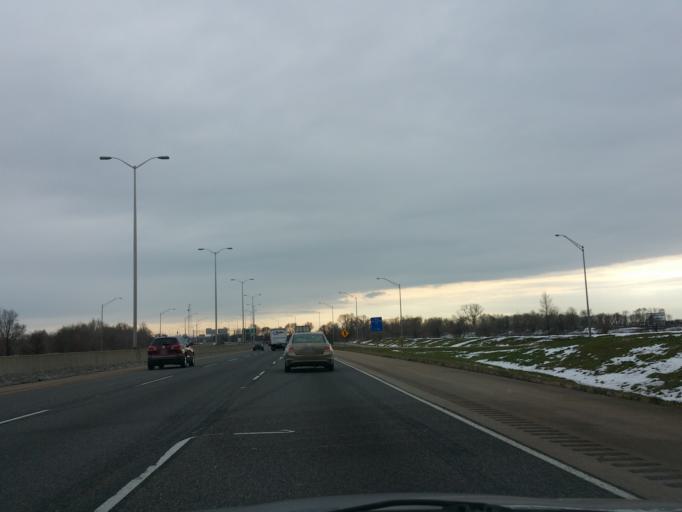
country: US
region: Illinois
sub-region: Winnebago County
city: Roscoe
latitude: 42.4555
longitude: -88.9952
